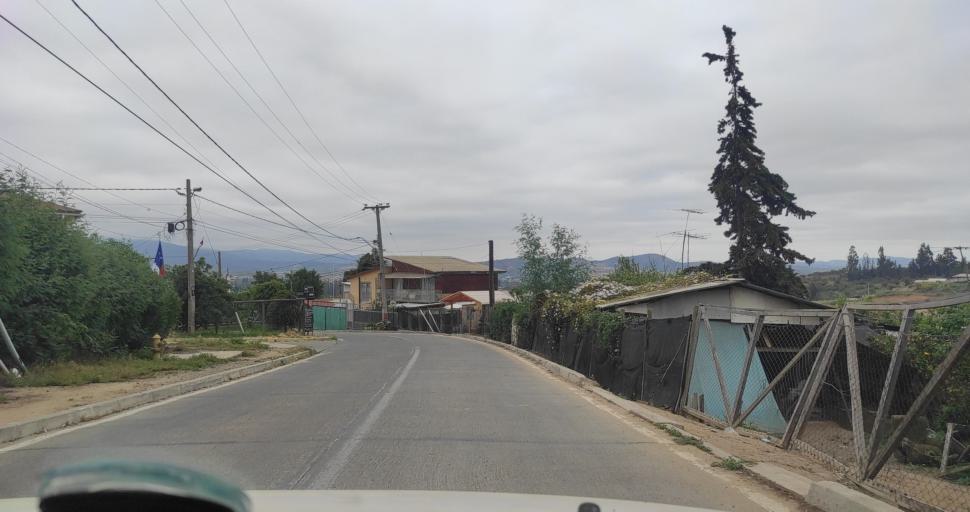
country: CL
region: Valparaiso
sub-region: Provincia de Marga Marga
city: Limache
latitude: -32.9905
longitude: -71.2259
